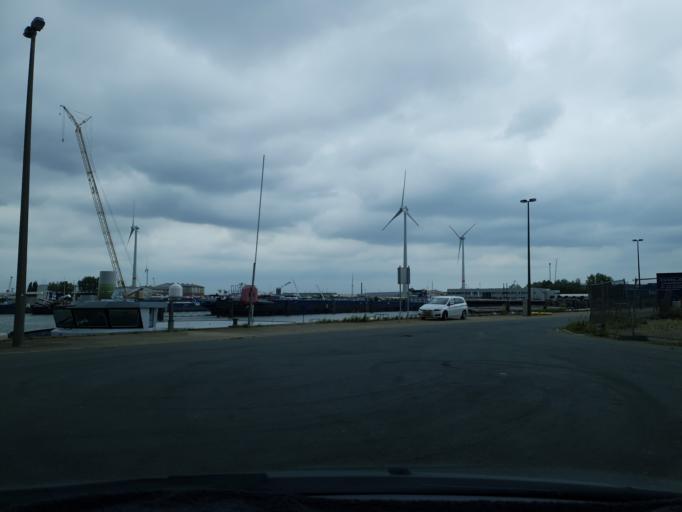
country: BE
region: Flanders
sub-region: Provincie Antwerpen
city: Antwerpen
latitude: 51.2475
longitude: 4.3921
